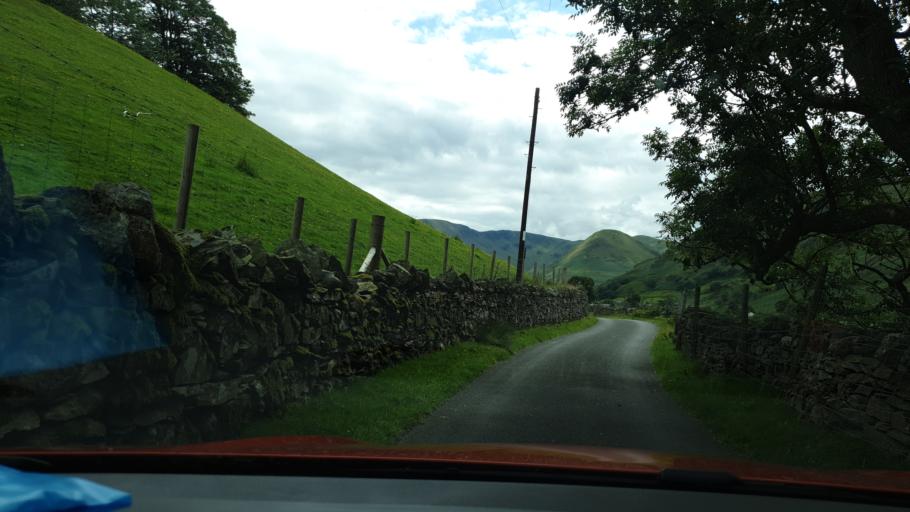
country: GB
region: England
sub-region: Cumbria
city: Ambleside
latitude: 54.5623
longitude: -2.8767
